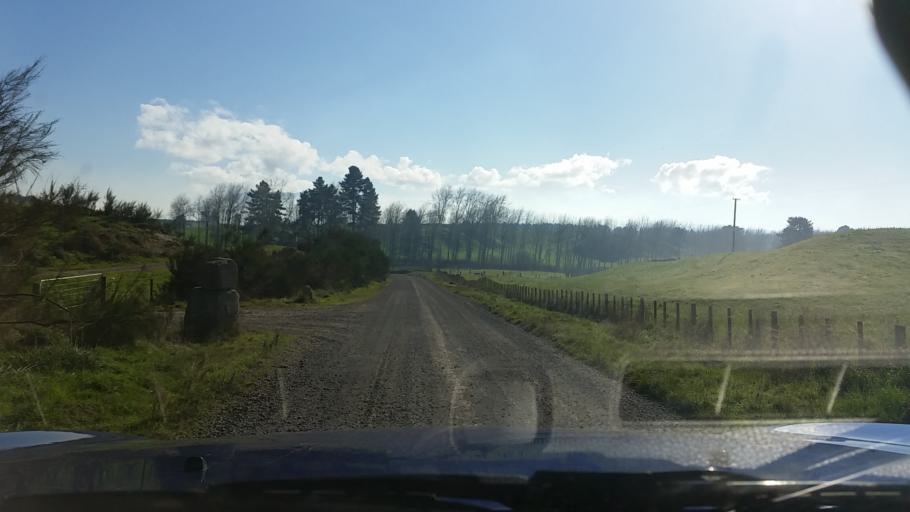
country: NZ
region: Bay of Plenty
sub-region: Whakatane District
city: Murupara
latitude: -38.3399
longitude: 176.5397
